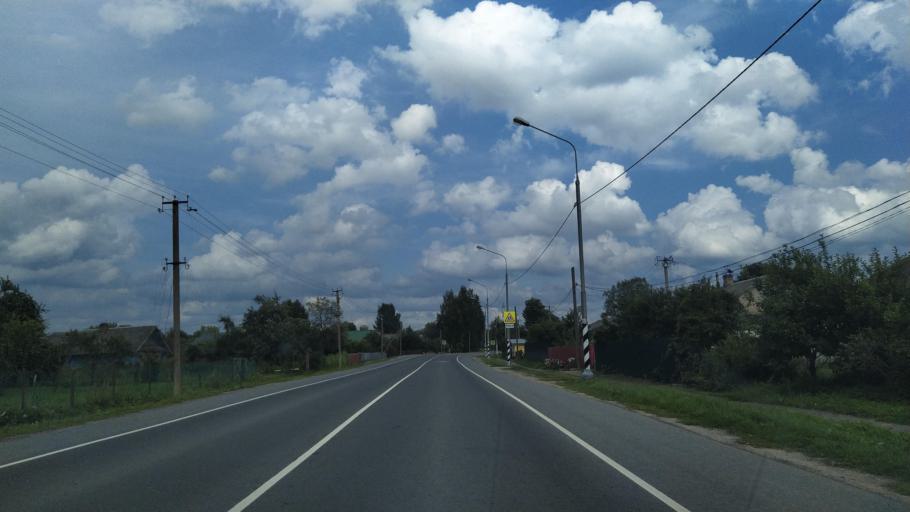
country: RU
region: Pskov
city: Dno
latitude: 58.0611
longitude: 29.9834
